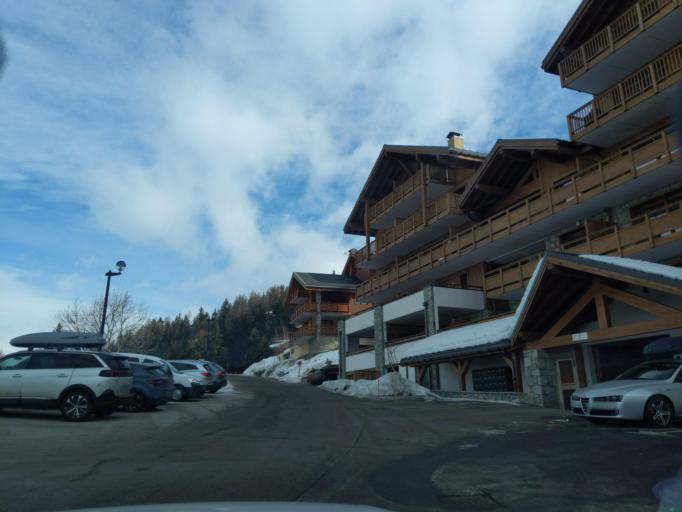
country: FR
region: Rhone-Alpes
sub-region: Departement de la Savoie
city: Bourg-Saint-Maurice
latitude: 45.5588
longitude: 6.7632
